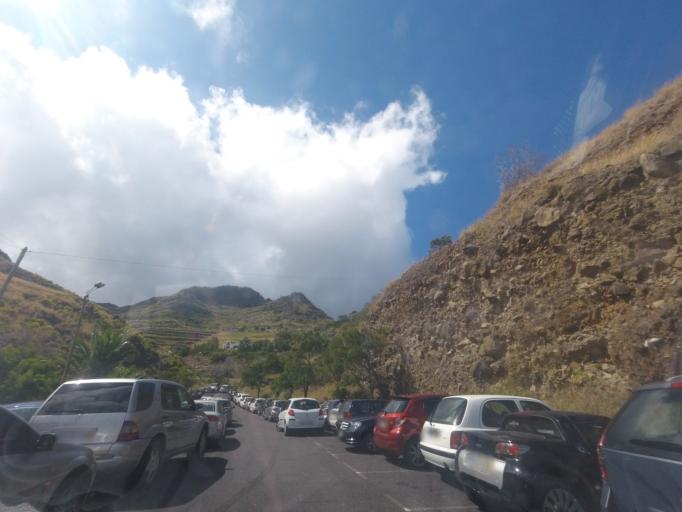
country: PT
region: Madeira
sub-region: Machico
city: Canical
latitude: 32.7356
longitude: -16.7459
